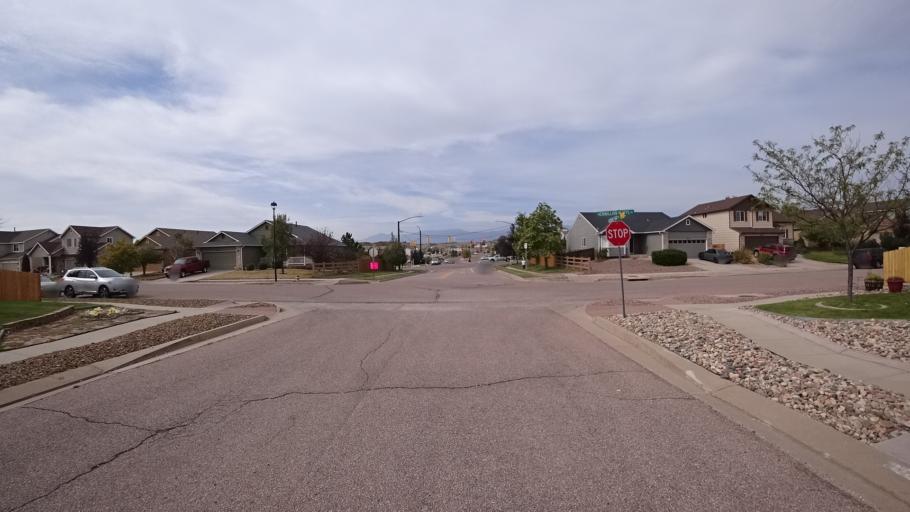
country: US
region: Colorado
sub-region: El Paso County
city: Cimarron Hills
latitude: 38.9136
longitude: -104.7147
